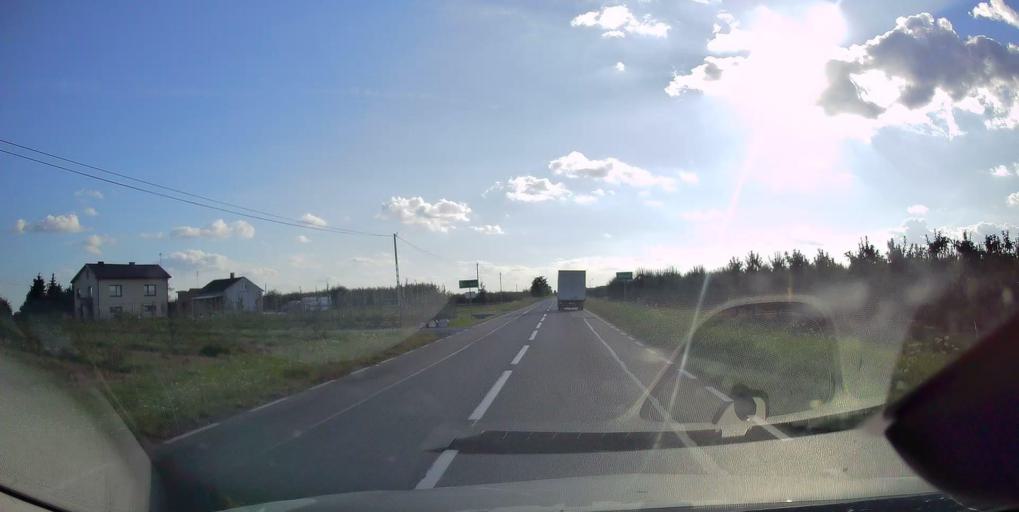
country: PL
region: Masovian Voivodeship
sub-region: Powiat grojecki
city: Bledow
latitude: 51.8069
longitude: 20.6569
